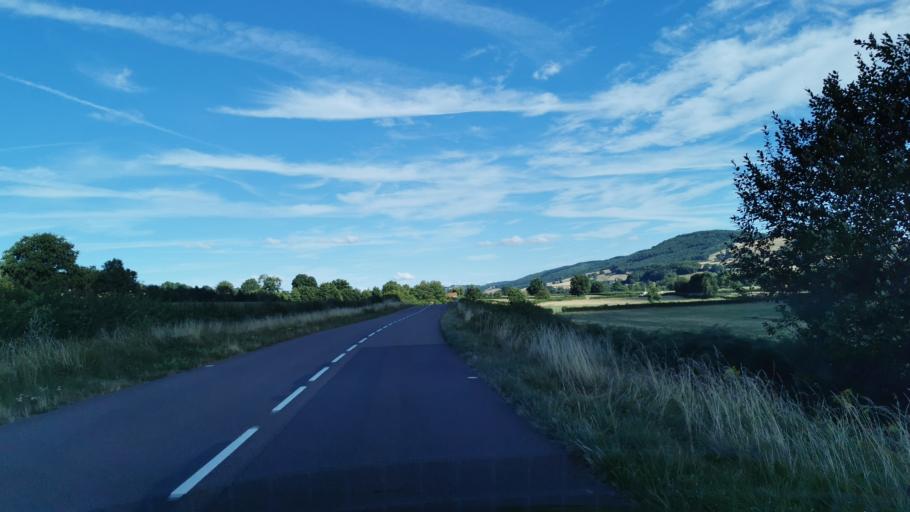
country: FR
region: Bourgogne
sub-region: Departement de Saone-et-Loire
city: Marmagne
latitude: 46.8596
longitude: 4.3083
